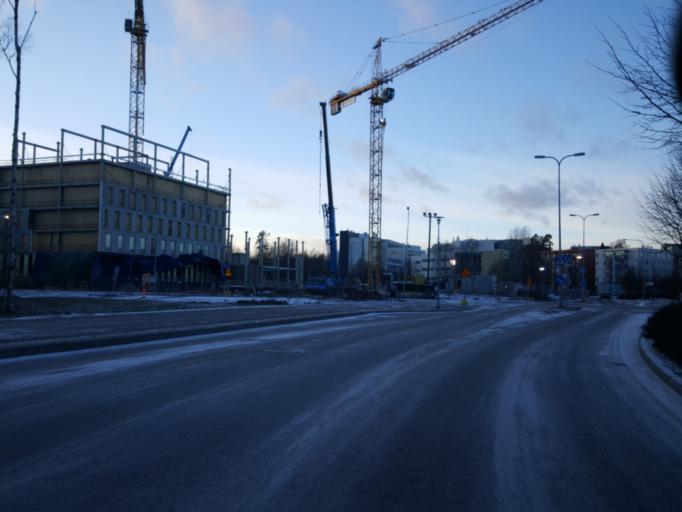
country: FI
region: Uusimaa
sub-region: Helsinki
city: Teekkarikylae
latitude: 60.2104
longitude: 24.8267
